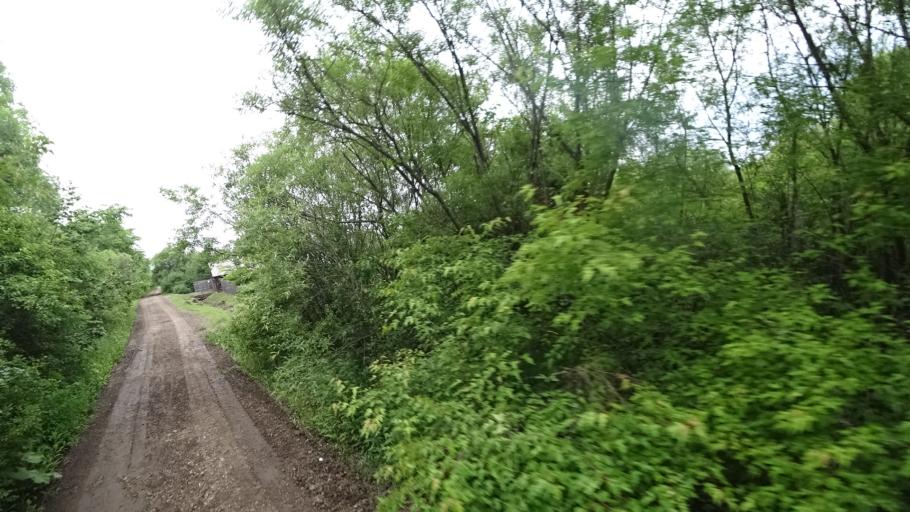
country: RU
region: Primorskiy
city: Novosysoyevka
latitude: 44.2425
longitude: 133.3756
